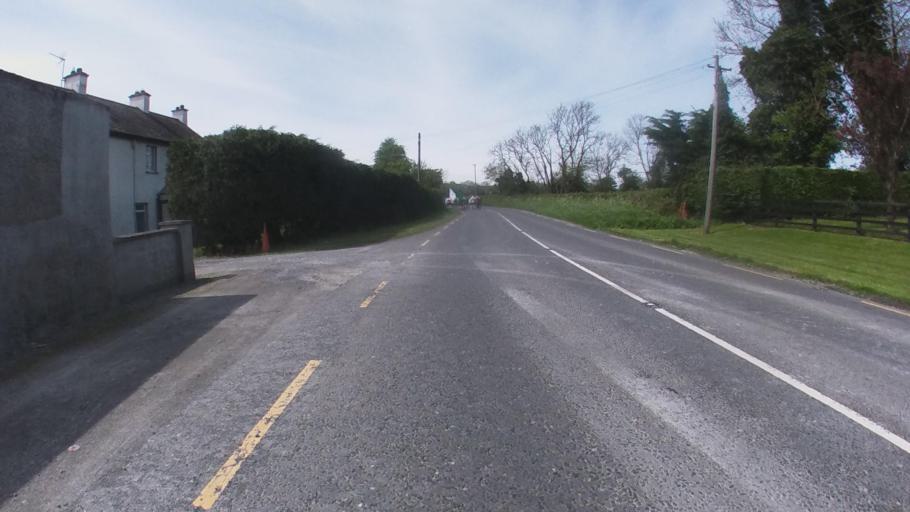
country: IE
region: Leinster
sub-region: County Carlow
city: Carlow
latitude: 52.8440
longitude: -6.9805
